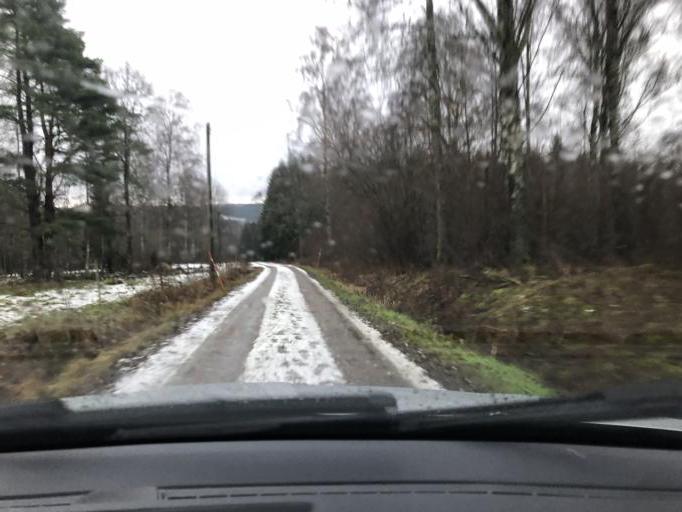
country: SE
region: Vaestra Goetaland
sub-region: Ulricehamns Kommun
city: Ulricehamn
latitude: 57.8241
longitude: 13.2779
